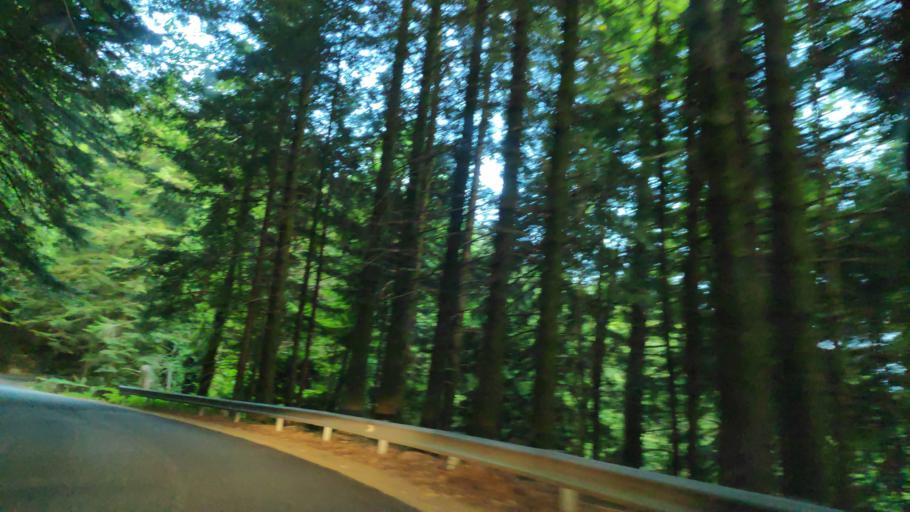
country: IT
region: Calabria
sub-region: Provincia di Vibo-Valentia
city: Mongiana
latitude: 38.5335
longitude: 16.3318
